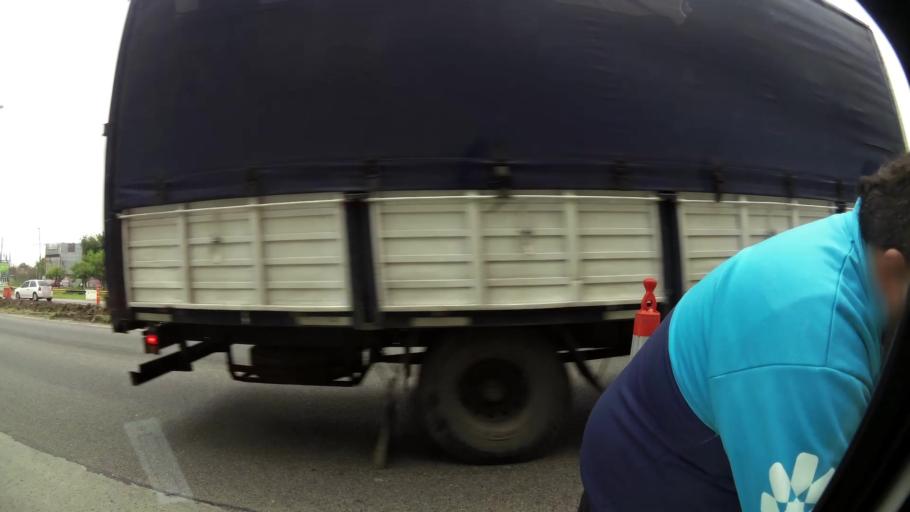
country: AR
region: Buenos Aires
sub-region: Partido de La Plata
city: La Plata
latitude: -34.8862
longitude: -57.9569
